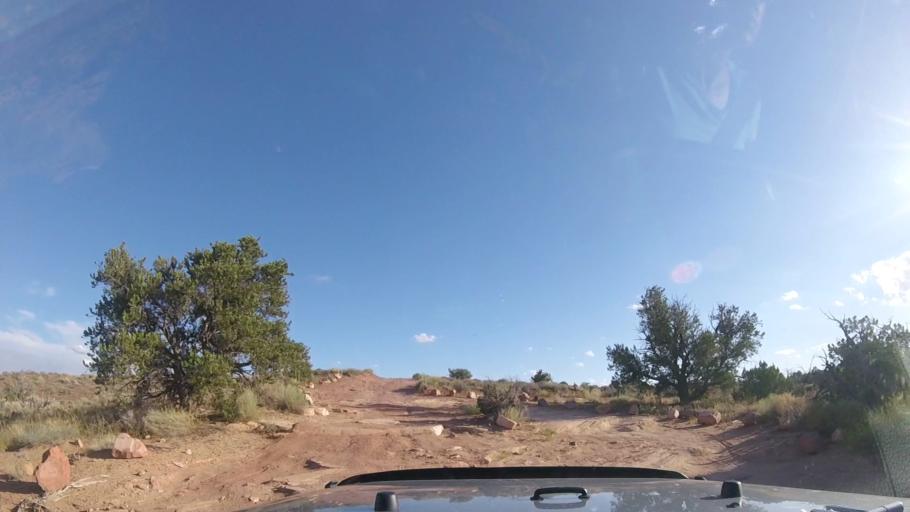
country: US
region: Utah
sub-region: Grand County
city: Moab
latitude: 38.2160
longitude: -109.8122
